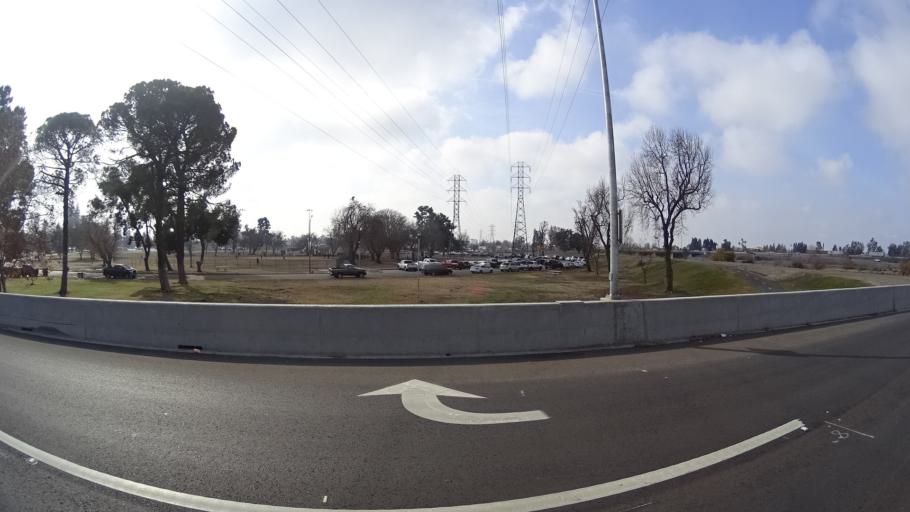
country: US
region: California
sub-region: Kern County
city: Bakersfield
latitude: 35.3815
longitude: -119.0399
